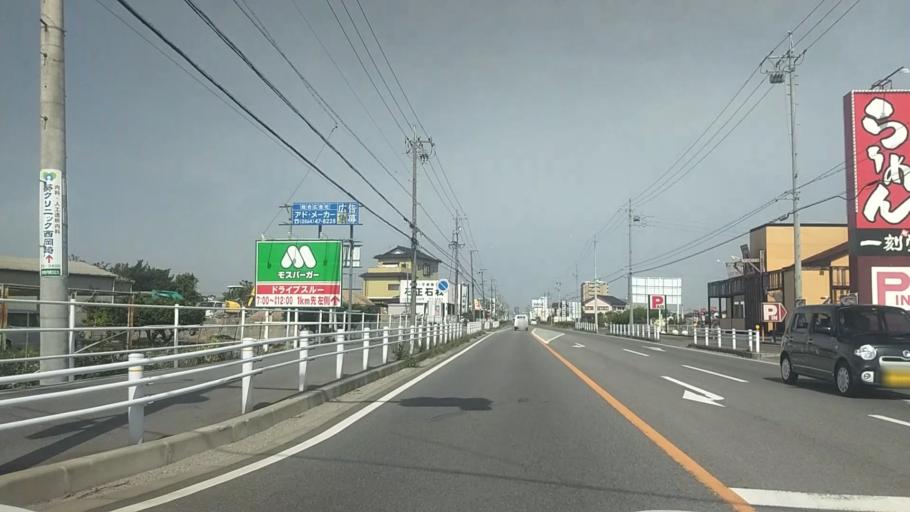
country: JP
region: Aichi
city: Okazaki
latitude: 34.9419
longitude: 137.1303
